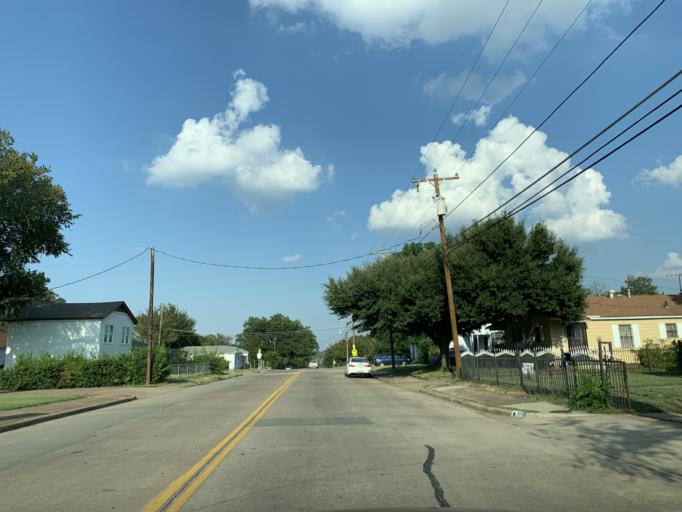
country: US
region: Texas
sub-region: Dallas County
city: Dallas
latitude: 32.7411
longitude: -96.7925
